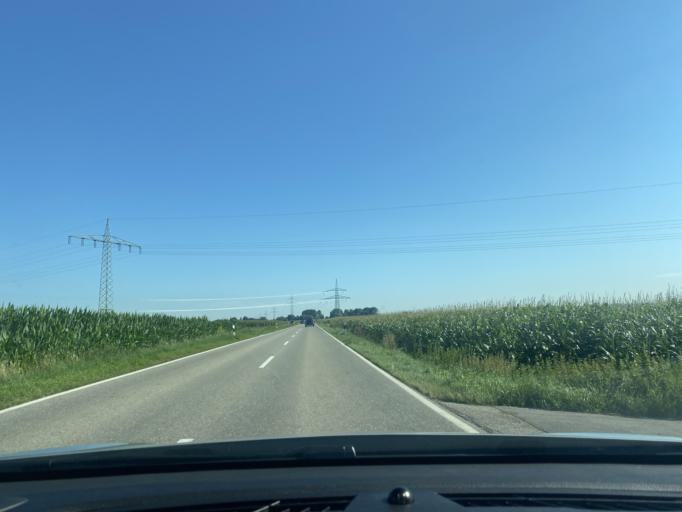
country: DE
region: Bavaria
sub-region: Upper Bavaria
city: Eitting
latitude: 48.3382
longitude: 11.8960
